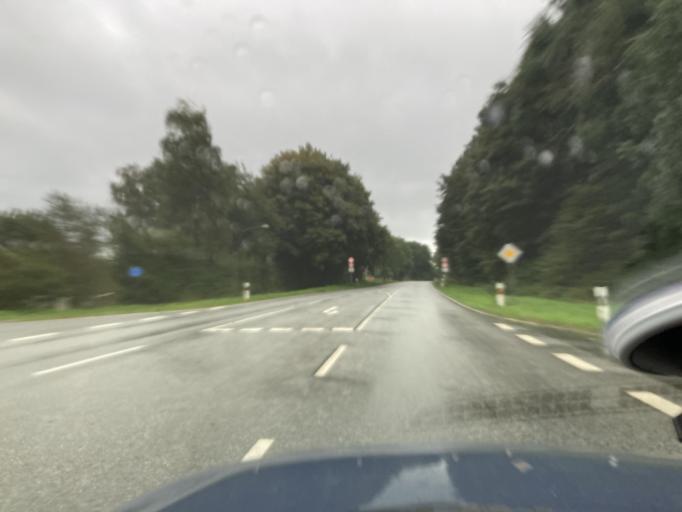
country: DE
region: Schleswig-Holstein
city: Gaushorn
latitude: 54.1964
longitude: 9.2142
